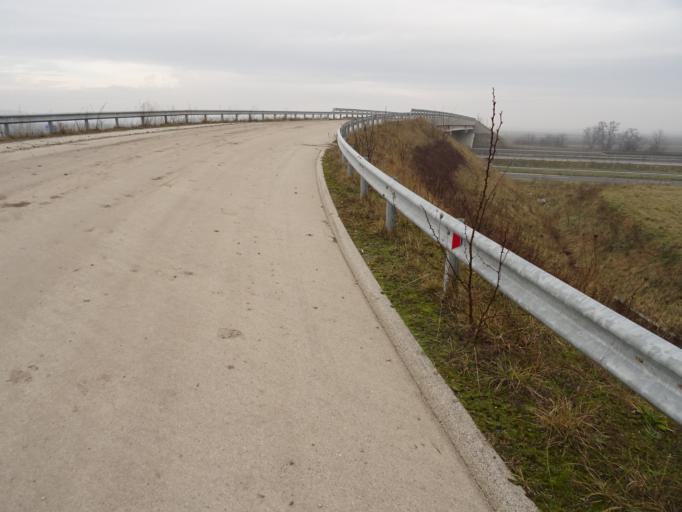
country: HU
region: Gyor-Moson-Sopron
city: Kony
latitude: 47.6380
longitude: 17.3715
